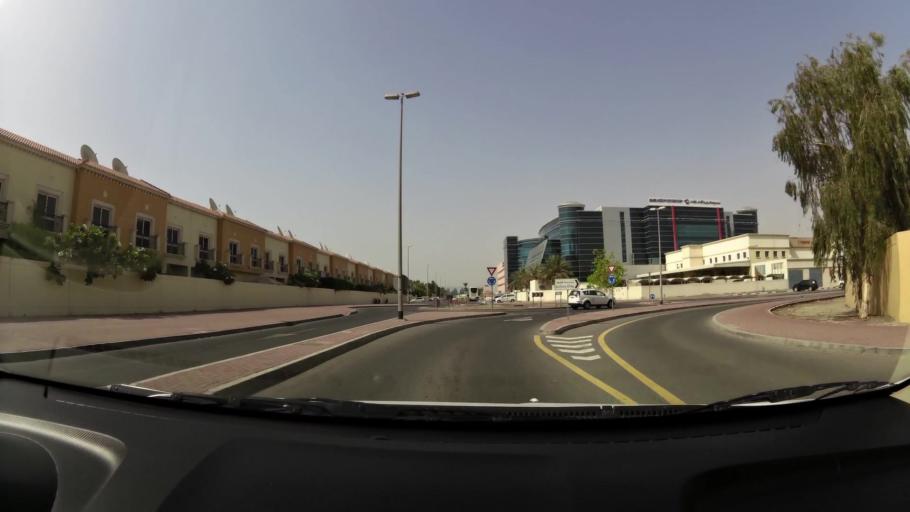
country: AE
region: Ash Shariqah
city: Sharjah
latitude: 25.2361
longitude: 55.3569
